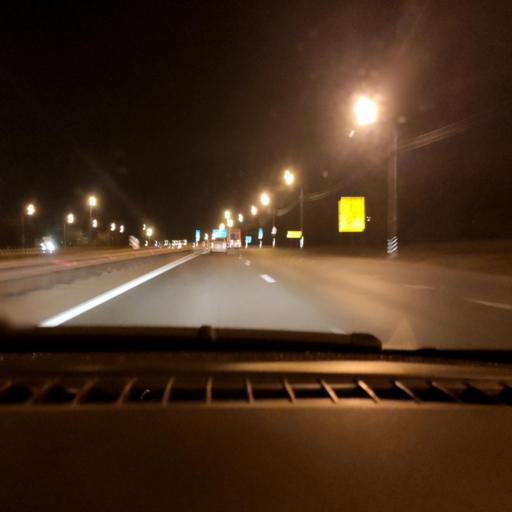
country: RU
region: Lipetsk
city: Khlevnoye
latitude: 52.1135
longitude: 39.1864
